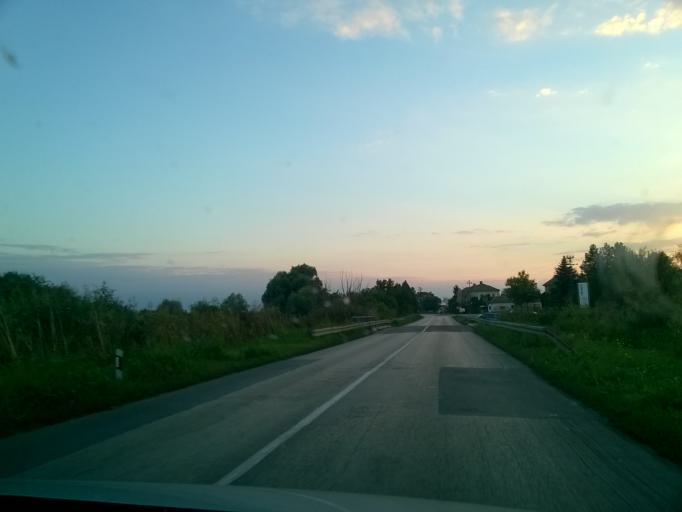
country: RS
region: Autonomna Pokrajina Vojvodina
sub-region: Juznobanatski Okrug
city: Pancevo
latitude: 44.9361
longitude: 20.6690
